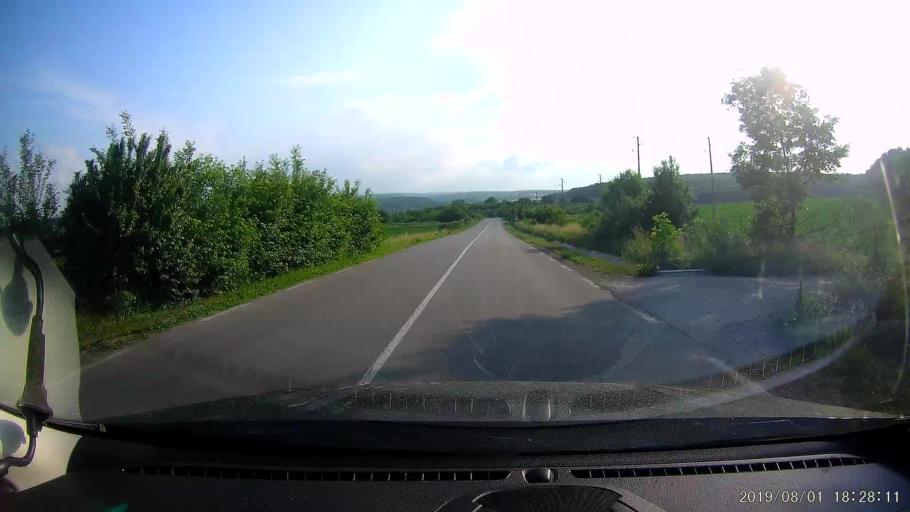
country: BG
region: Shumen
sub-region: Obshtina Venets
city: Venets
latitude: 43.5779
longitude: 26.9688
